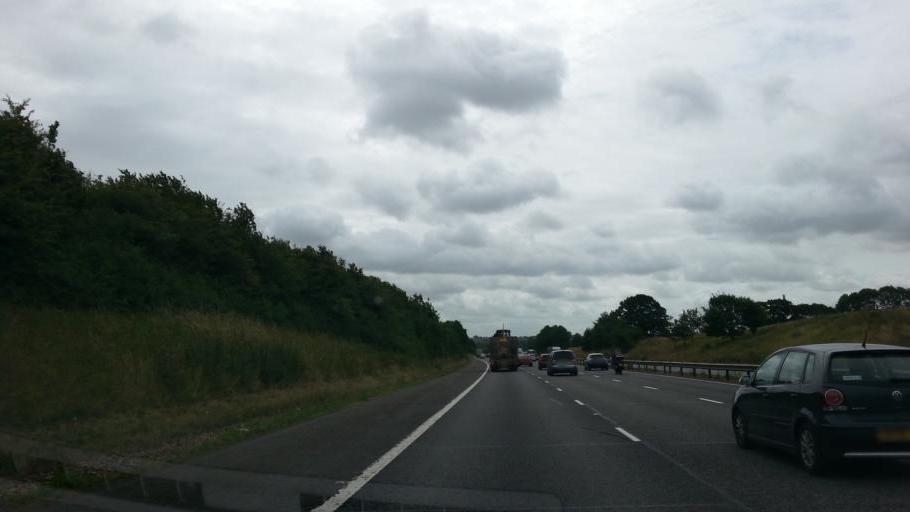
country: GB
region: England
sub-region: Oxfordshire
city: Adderbury
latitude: 52.0199
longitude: -1.2899
